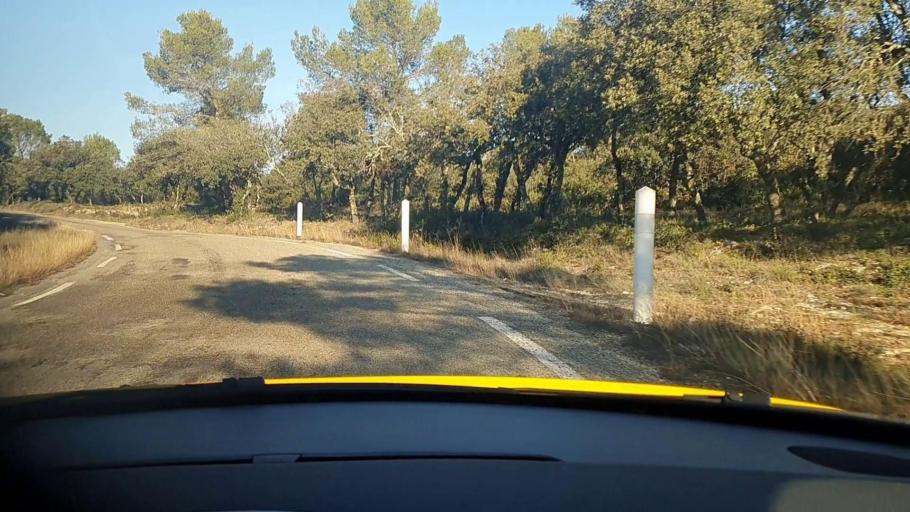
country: FR
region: Languedoc-Roussillon
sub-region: Departement du Gard
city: Goudargues
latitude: 44.1594
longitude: 4.3533
